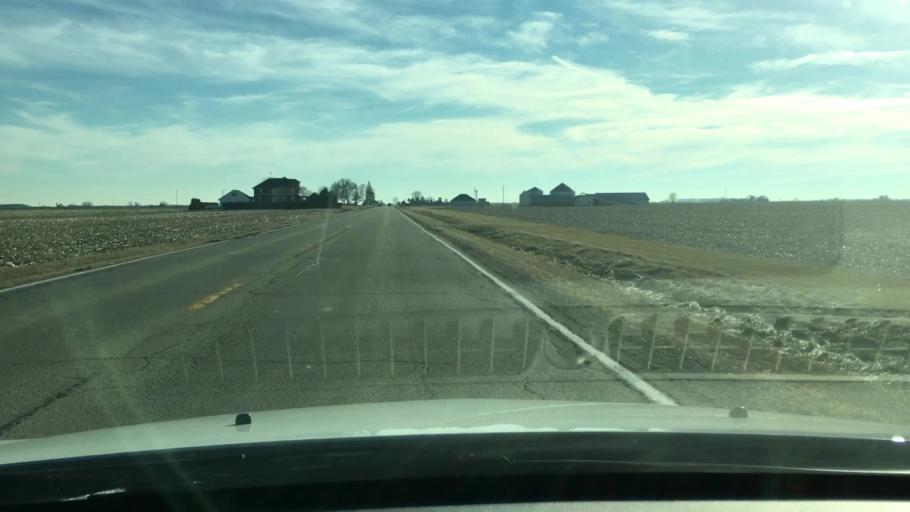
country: US
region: Illinois
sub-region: LaSalle County
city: Peru
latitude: 41.4151
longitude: -89.1263
